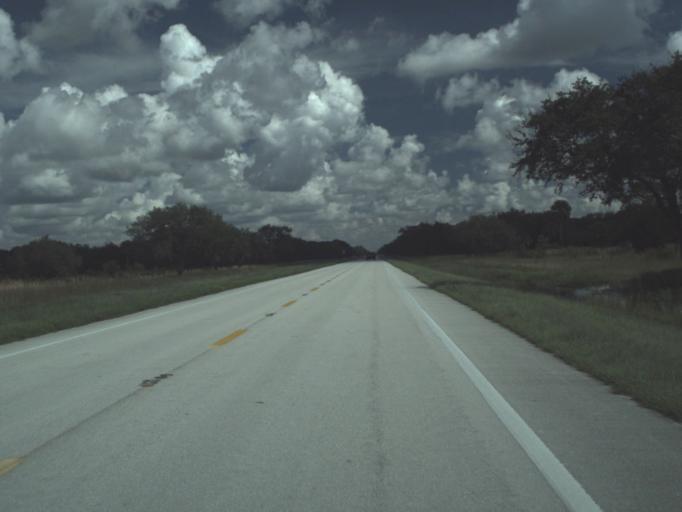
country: US
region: Florida
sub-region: Hendry County
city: Port LaBelle
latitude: 26.8573
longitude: -81.3740
